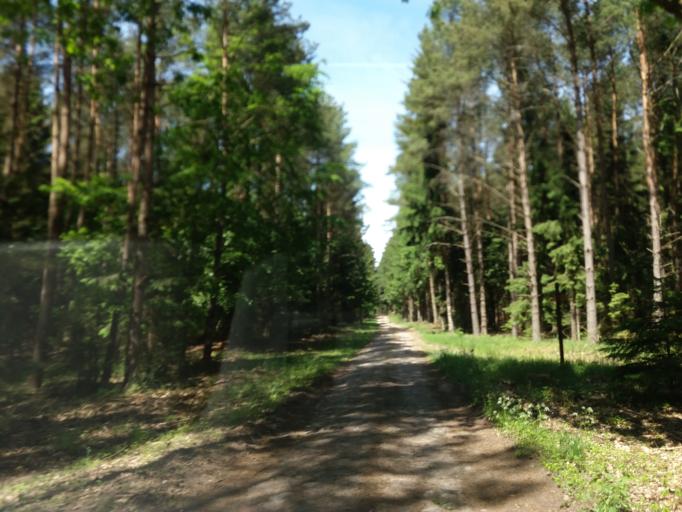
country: PL
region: West Pomeranian Voivodeship
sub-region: Powiat choszczenski
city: Recz
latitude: 53.3294
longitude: 15.5262
